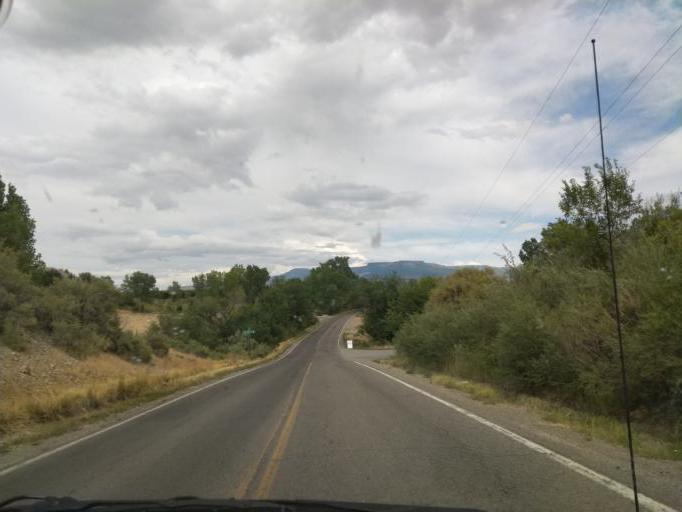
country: US
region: Colorado
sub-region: Mesa County
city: Clifton
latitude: 39.0558
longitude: -108.4432
